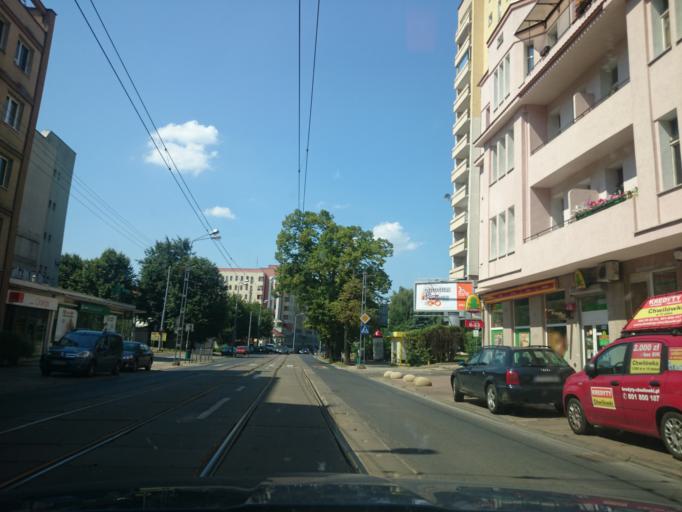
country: PL
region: West Pomeranian Voivodeship
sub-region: Szczecin
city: Szczecin
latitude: 53.4411
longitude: 14.5497
